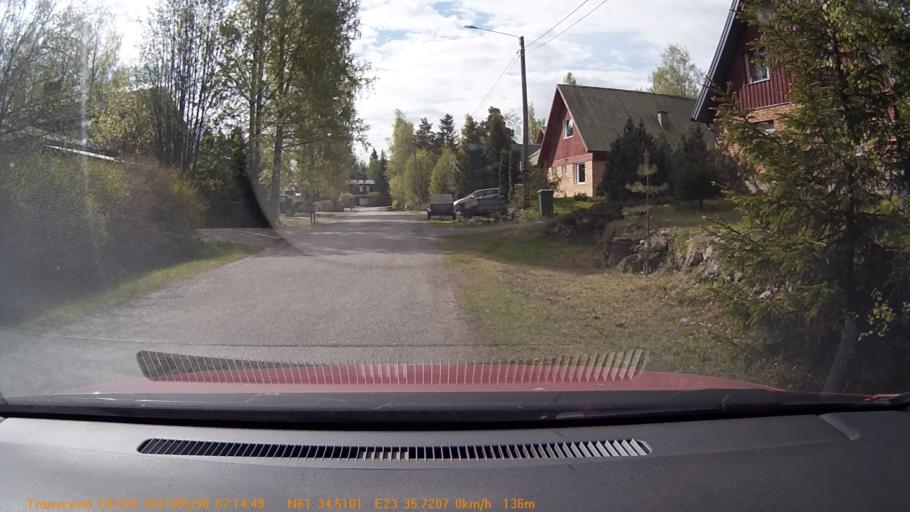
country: FI
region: Pirkanmaa
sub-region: Tampere
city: Yloejaervi
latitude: 61.5752
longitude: 23.5953
